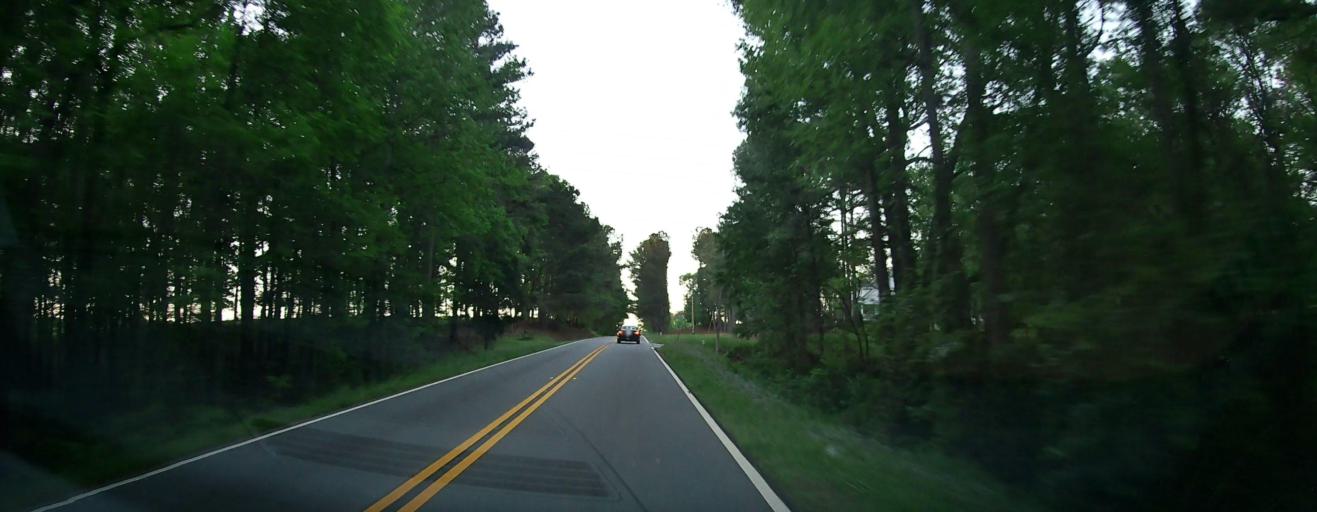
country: US
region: Georgia
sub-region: Henry County
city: McDonough
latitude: 33.4697
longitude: -84.1945
